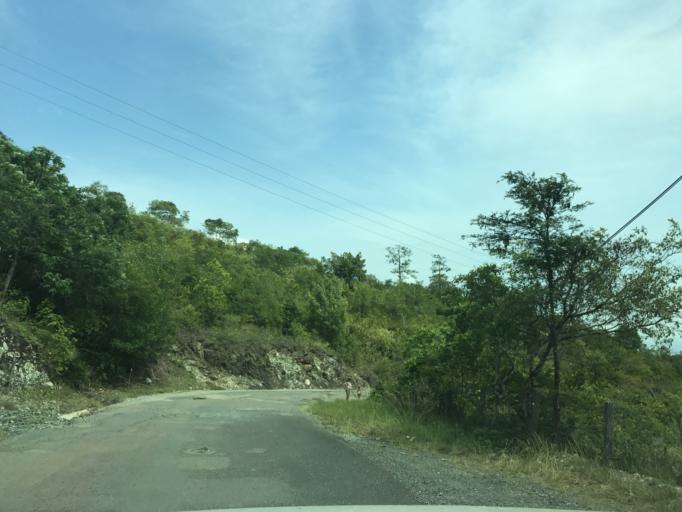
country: GT
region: Izabal
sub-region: Municipio de Los Amates
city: Los Amates
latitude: 15.3835
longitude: -89.0209
